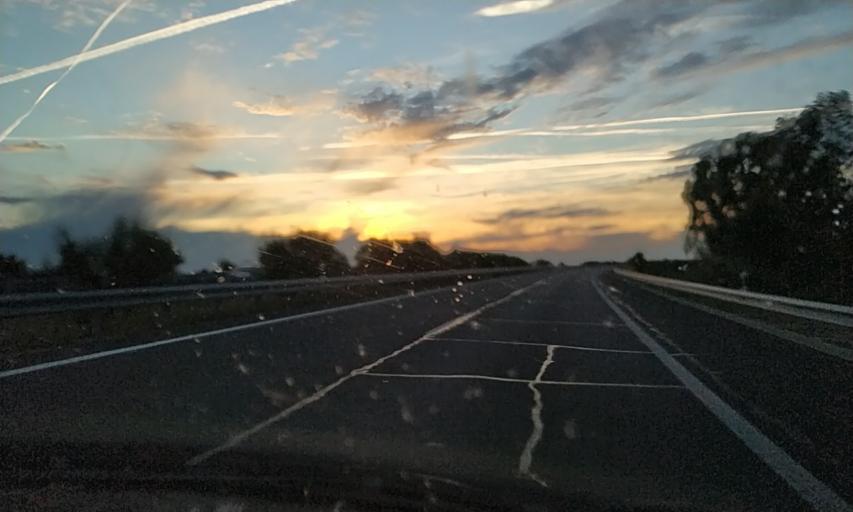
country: ES
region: Extremadura
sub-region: Provincia de Caceres
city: Caceres
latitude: 39.4009
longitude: -6.3919
